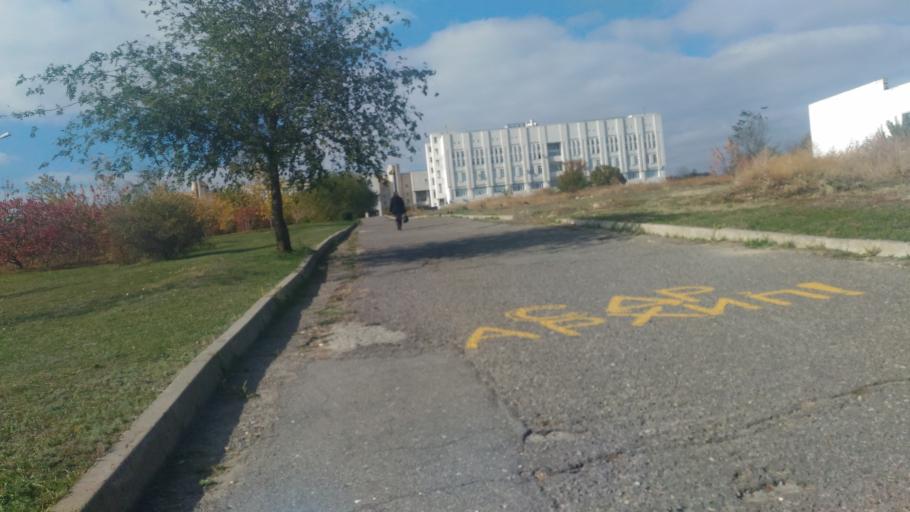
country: RU
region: Volgograd
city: Volgograd
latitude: 48.6413
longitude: 44.4275
